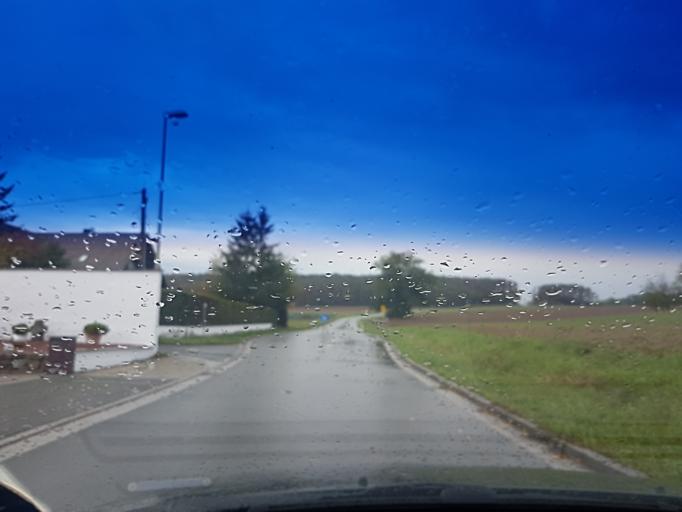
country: DE
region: Bavaria
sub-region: Regierungsbezirk Mittelfranken
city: Wachenroth
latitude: 49.7529
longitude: 10.6666
